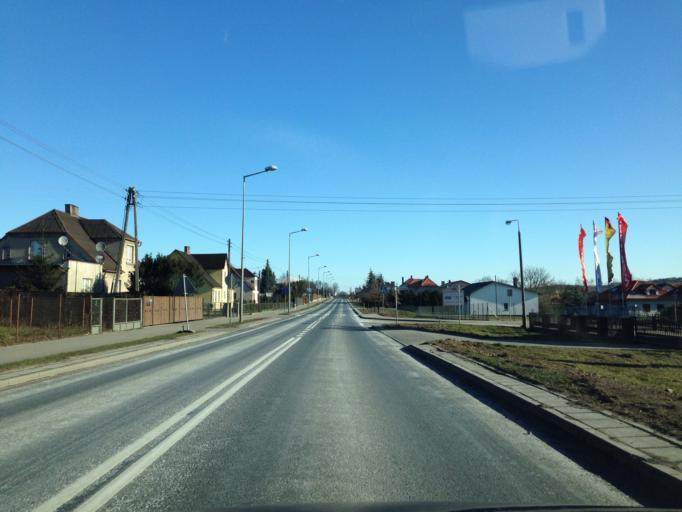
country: PL
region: Warmian-Masurian Voivodeship
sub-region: Powiat nowomiejski
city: Nowe Miasto Lubawskie
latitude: 53.4358
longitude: 19.5921
